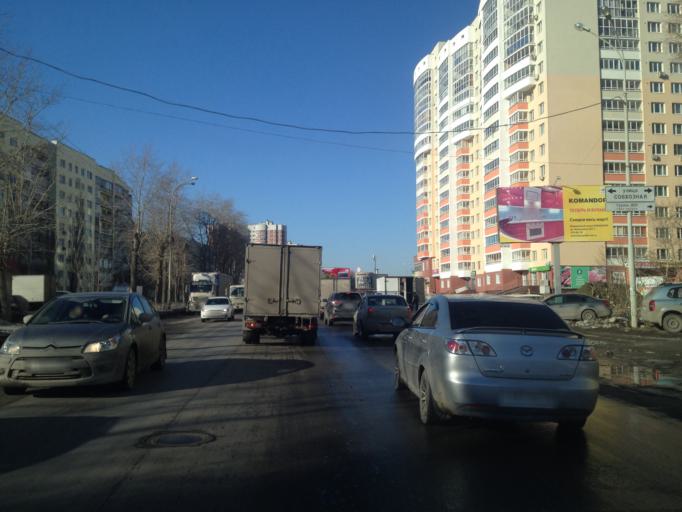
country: RU
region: Sverdlovsk
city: Yekaterinburg
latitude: 56.9058
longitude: 60.6217
